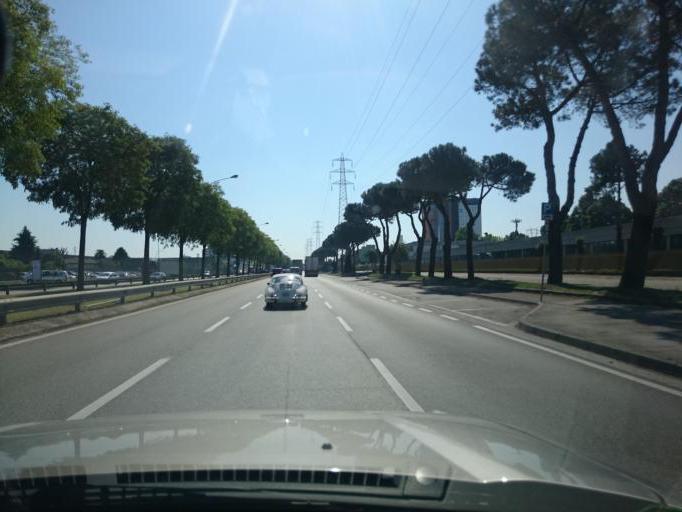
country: IT
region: Veneto
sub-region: Provincia di Padova
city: Noventa
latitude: 45.3933
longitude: 11.9371
